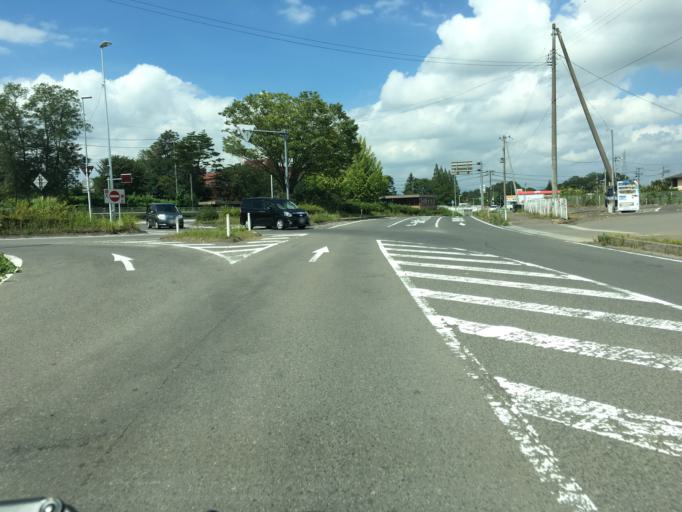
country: JP
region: Fukushima
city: Fukushima-shi
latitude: 37.6938
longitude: 140.4619
